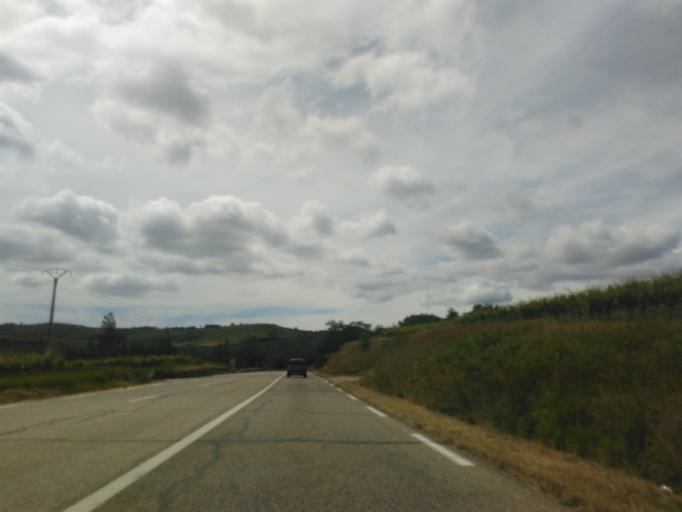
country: FR
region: Rhone-Alpes
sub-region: Departement de l'Ardeche
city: Alba-la-Romaine
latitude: 44.5827
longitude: 4.5694
